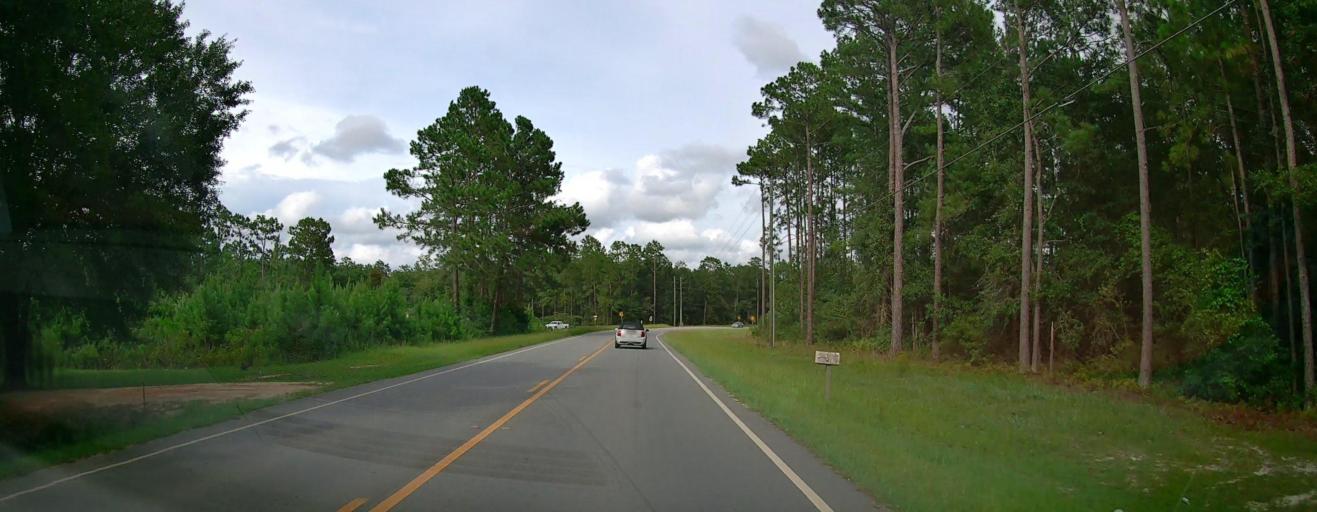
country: US
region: Georgia
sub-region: Wayne County
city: Jesup
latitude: 31.6661
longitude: -81.8764
